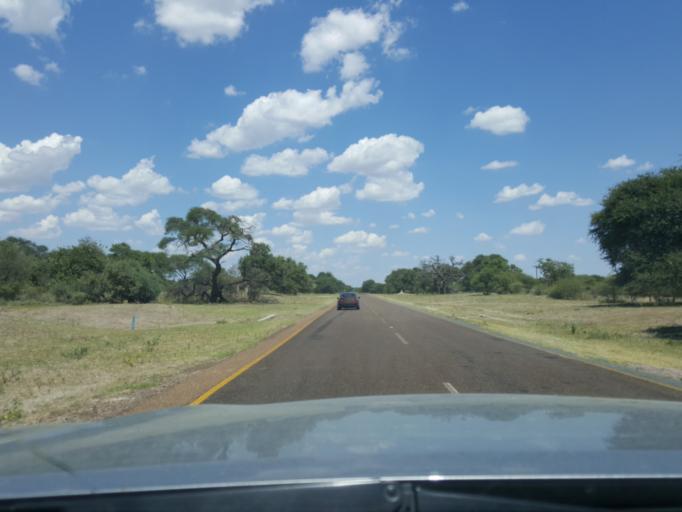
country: BW
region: North West
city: Maun
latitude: -20.1792
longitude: 23.2500
